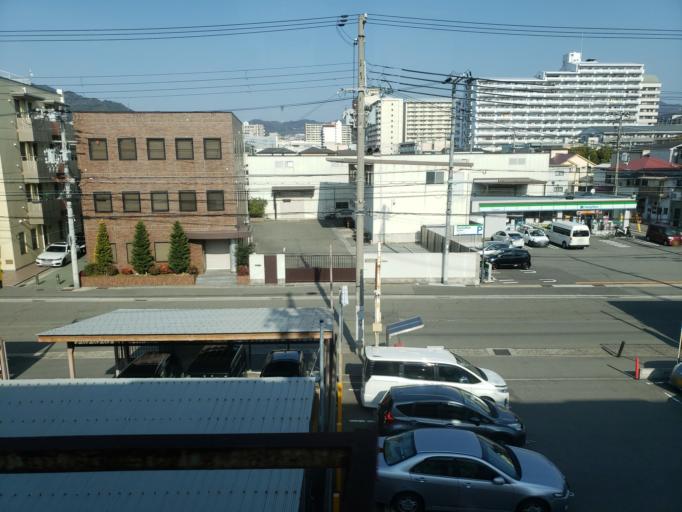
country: JP
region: Hyogo
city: Kobe
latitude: 34.6642
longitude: 135.1573
